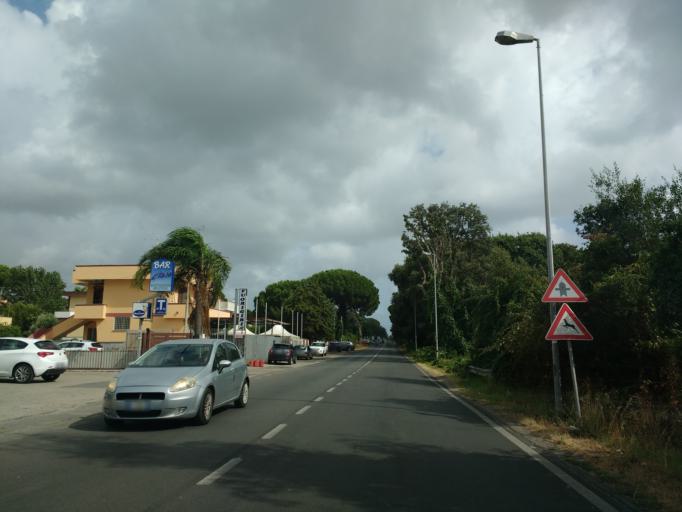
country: IT
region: Latium
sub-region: Citta metropolitana di Roma Capitale
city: Lavinio
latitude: 41.4902
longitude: 12.5967
